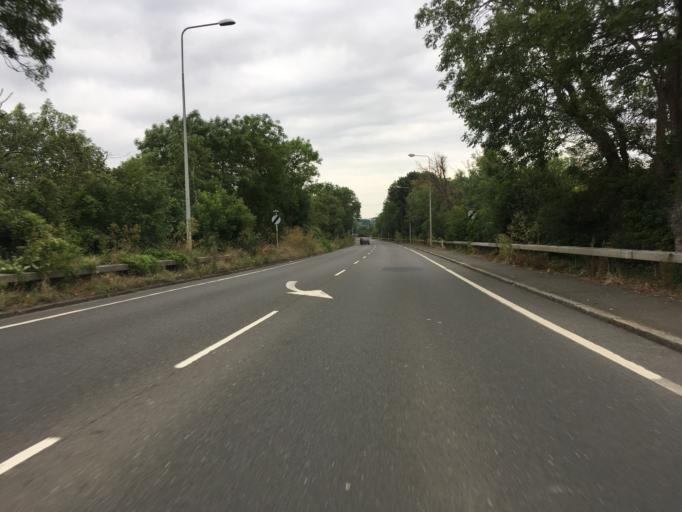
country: GB
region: England
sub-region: Central Bedfordshire
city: Houghton Regis
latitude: 51.9041
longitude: -0.5476
